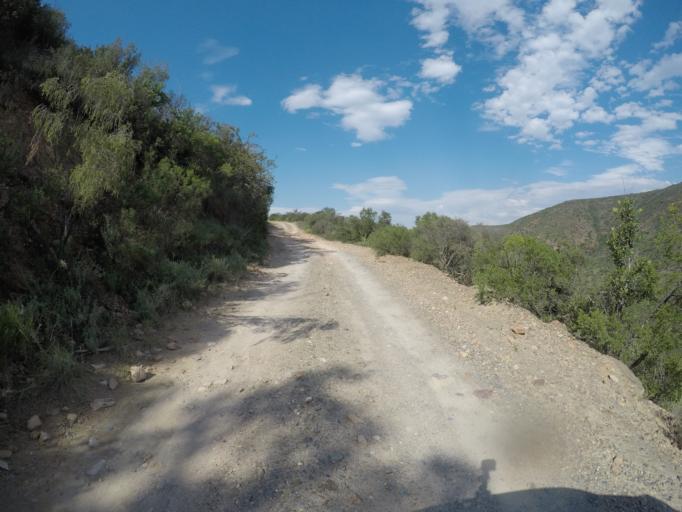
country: ZA
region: Eastern Cape
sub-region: Cacadu District Municipality
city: Kareedouw
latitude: -33.6500
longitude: 24.3504
